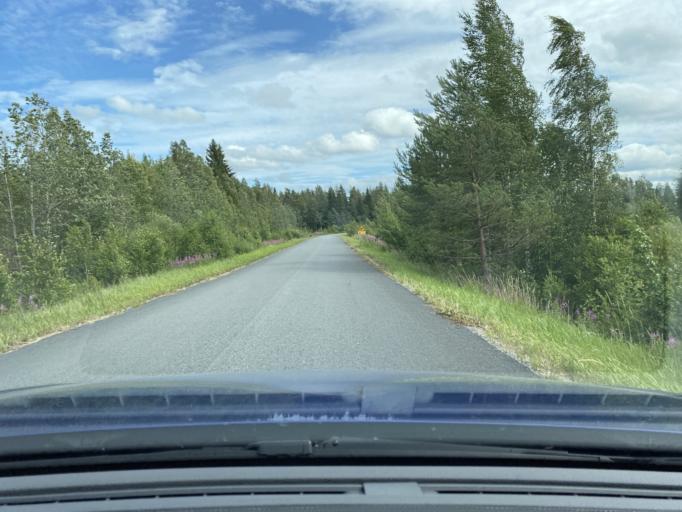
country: FI
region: Southern Ostrobothnia
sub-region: Seinaejoki
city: Jurva
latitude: 62.6266
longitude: 22.0238
